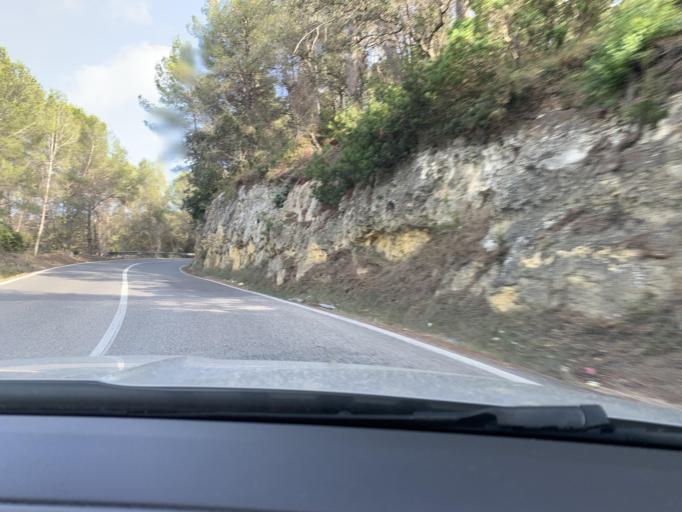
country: ES
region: Catalonia
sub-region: Provincia de Tarragona
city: el Catllar
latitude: 41.1494
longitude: 1.3139
